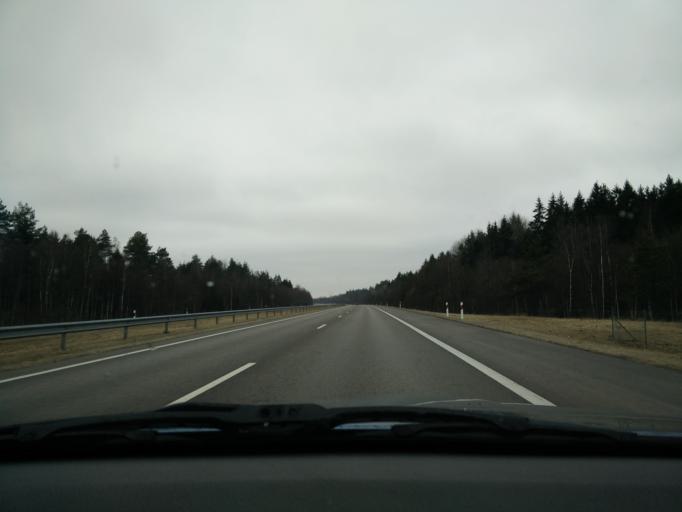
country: LT
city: Silale
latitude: 55.6066
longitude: 22.0859
